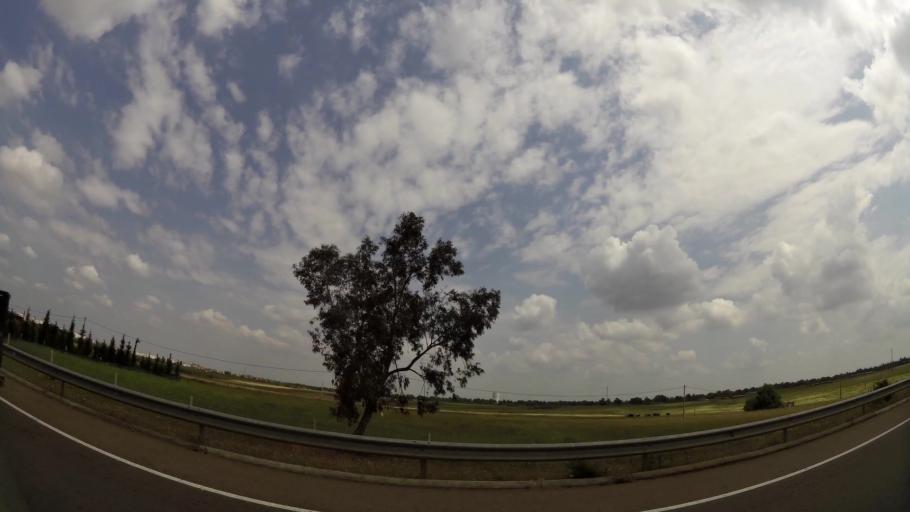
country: MA
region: Rabat-Sale-Zemmour-Zaer
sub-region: Khemisset
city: Tiflet
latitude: 33.9793
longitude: -6.5212
